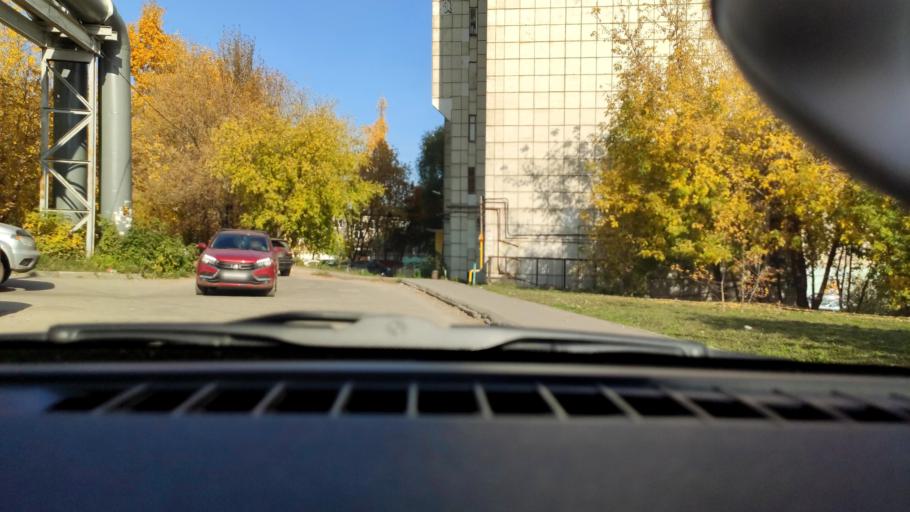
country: RU
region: Perm
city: Perm
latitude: 57.9964
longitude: 56.2730
